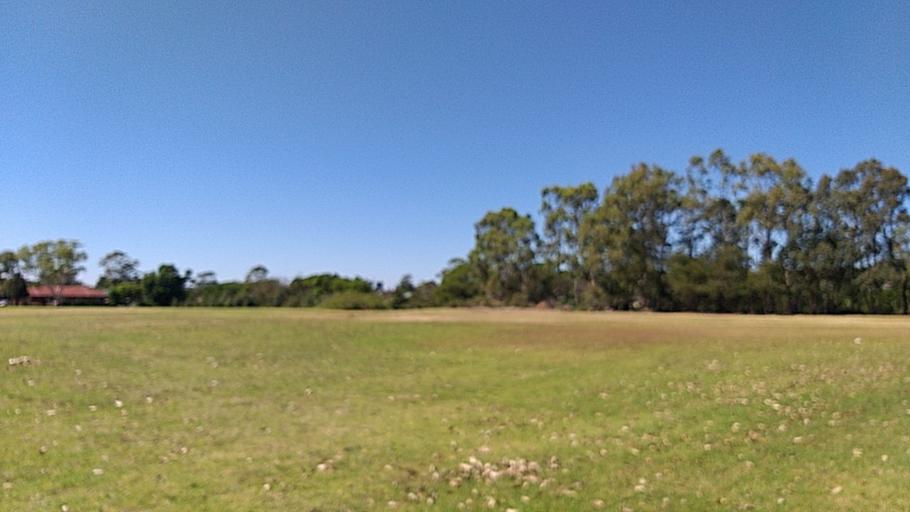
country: AU
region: New South Wales
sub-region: Wollongong
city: Fairy Meadow
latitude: -34.3914
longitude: 150.8892
